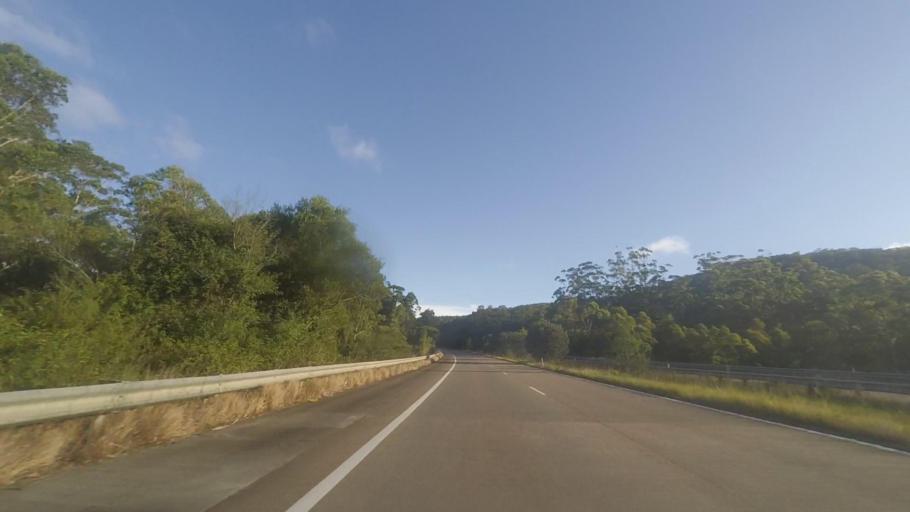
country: AU
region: New South Wales
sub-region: Great Lakes
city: Bulahdelah
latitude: -32.2739
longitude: 152.3289
